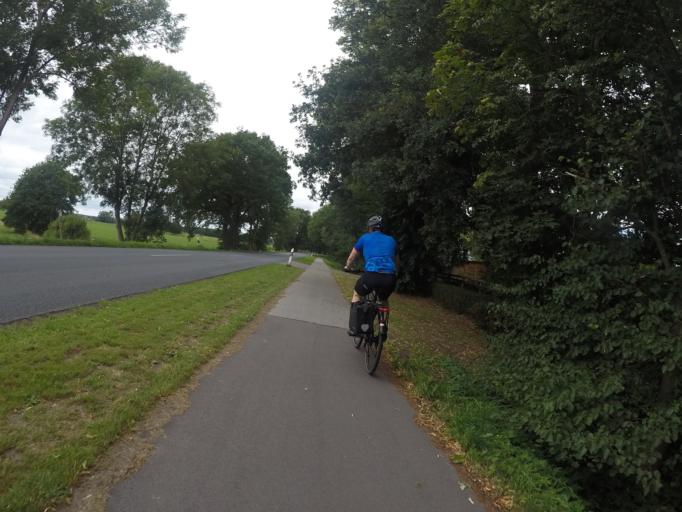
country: DE
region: Lower Saxony
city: Himmelpforten
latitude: 53.6329
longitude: 9.3013
